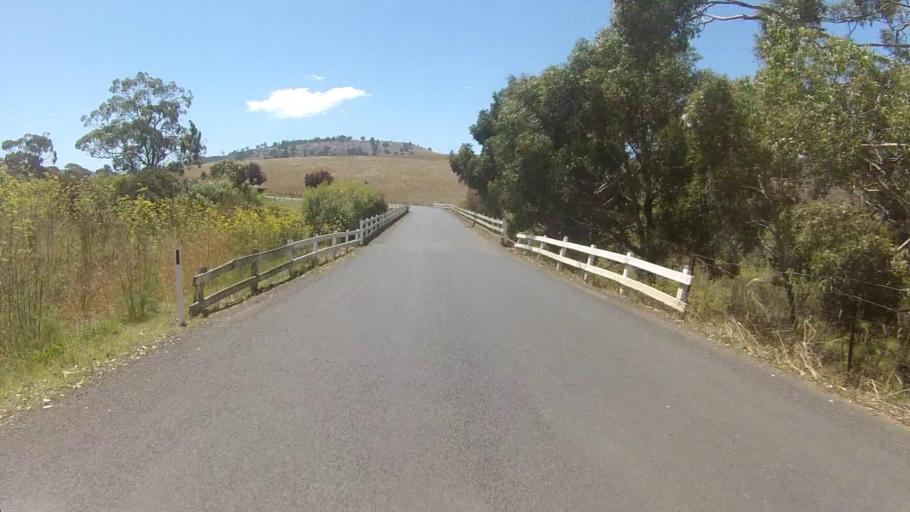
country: AU
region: Tasmania
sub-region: Sorell
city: Sorell
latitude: -42.7720
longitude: 147.5946
